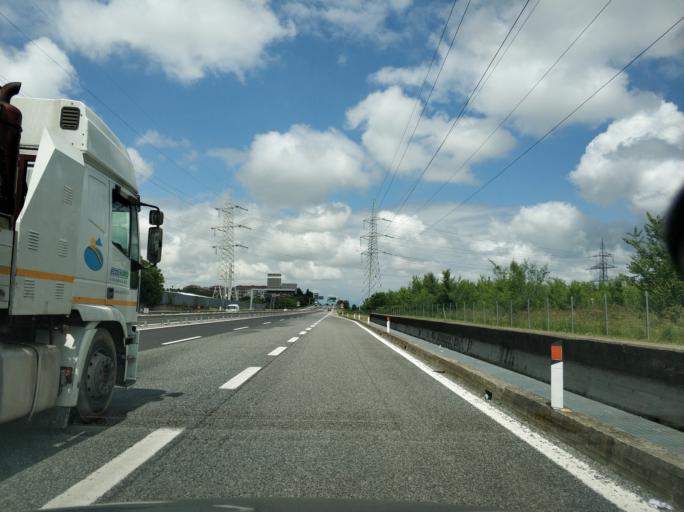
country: IT
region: Piedmont
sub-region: Provincia di Torino
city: Settimo Torinese
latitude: 45.1192
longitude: 7.7343
